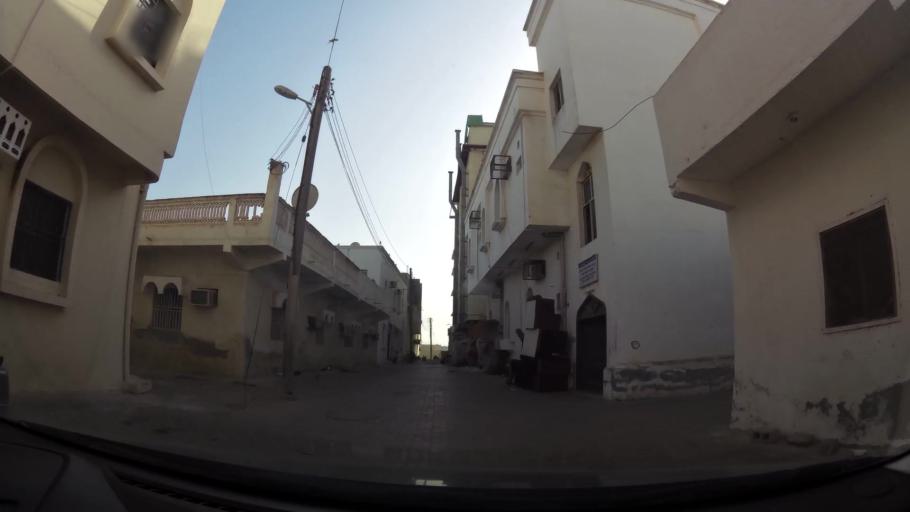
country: OM
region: Zufar
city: Salalah
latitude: 17.0104
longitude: 54.0785
